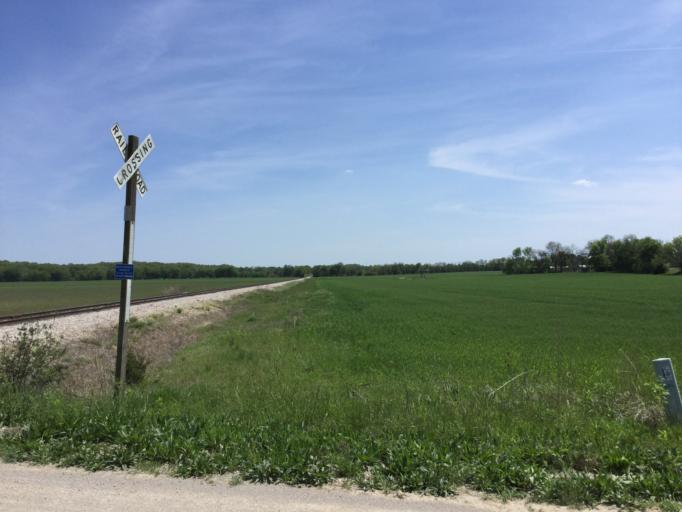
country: US
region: Kansas
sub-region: Montgomery County
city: Cherryvale
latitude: 37.3146
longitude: -95.5838
